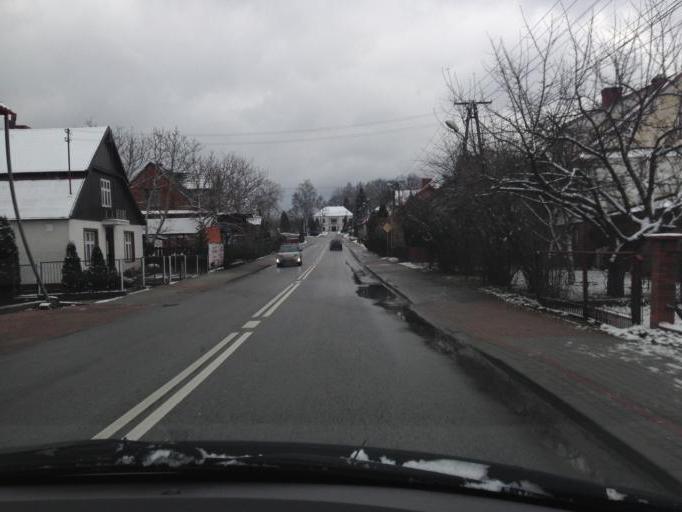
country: PL
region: Lesser Poland Voivodeship
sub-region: Powiat brzeski
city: Iwkowa
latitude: 49.8587
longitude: 20.5296
